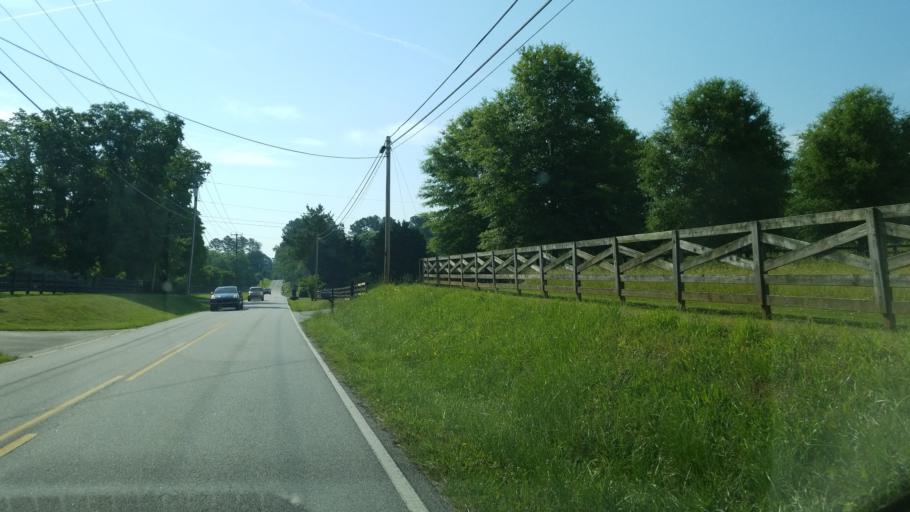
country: US
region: Tennessee
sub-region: Hamilton County
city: Collegedale
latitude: 35.0612
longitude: -85.0228
